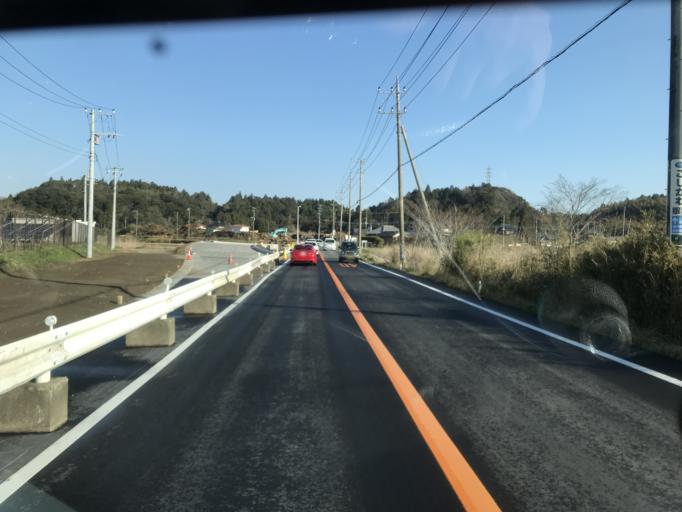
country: JP
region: Chiba
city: Sawara
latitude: 35.8744
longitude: 140.4953
